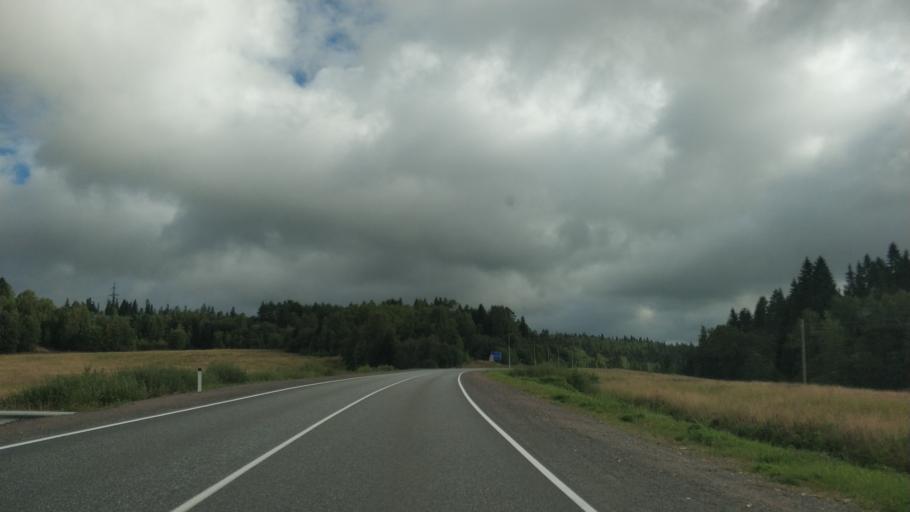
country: RU
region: Republic of Karelia
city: Khelyulya
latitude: 61.7726
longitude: 30.6555
